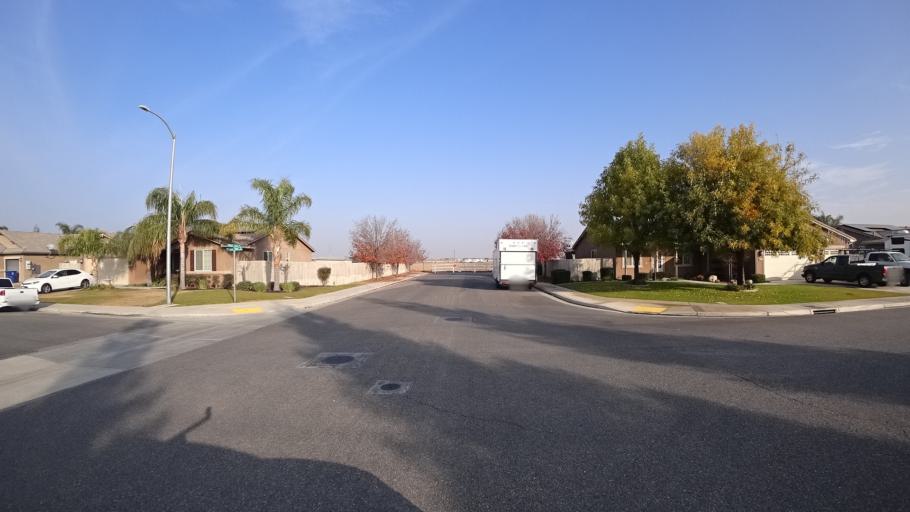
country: US
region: California
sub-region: Kern County
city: Greenacres
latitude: 35.4374
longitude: -119.1122
